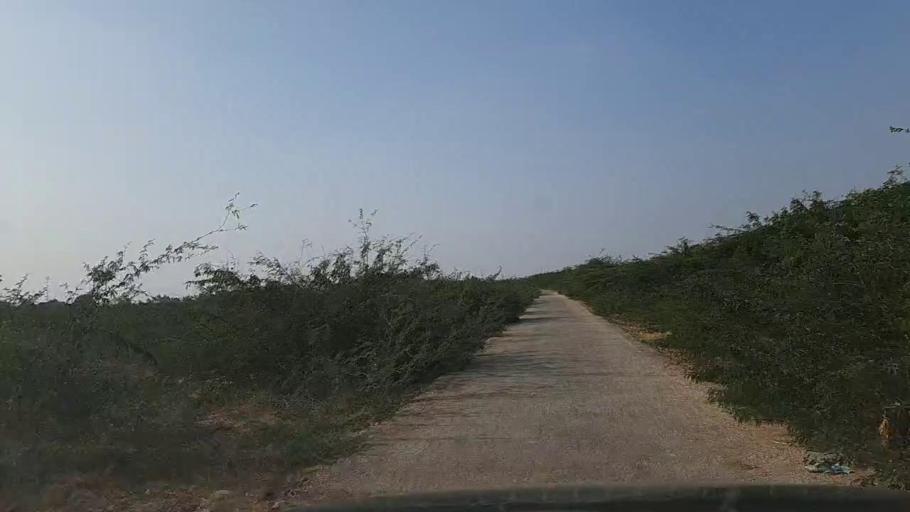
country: PK
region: Sindh
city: Gharo
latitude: 24.7553
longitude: 67.5300
